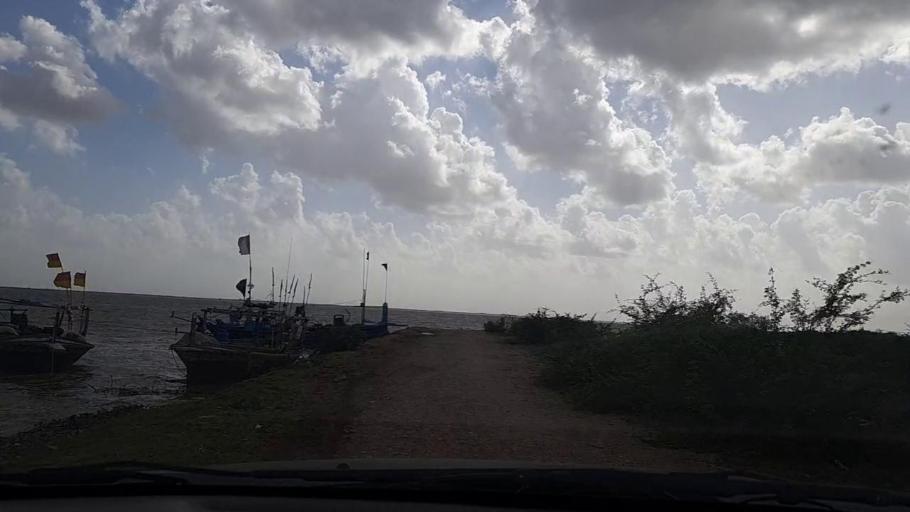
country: PK
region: Sindh
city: Keti Bandar
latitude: 24.0850
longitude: 67.6140
